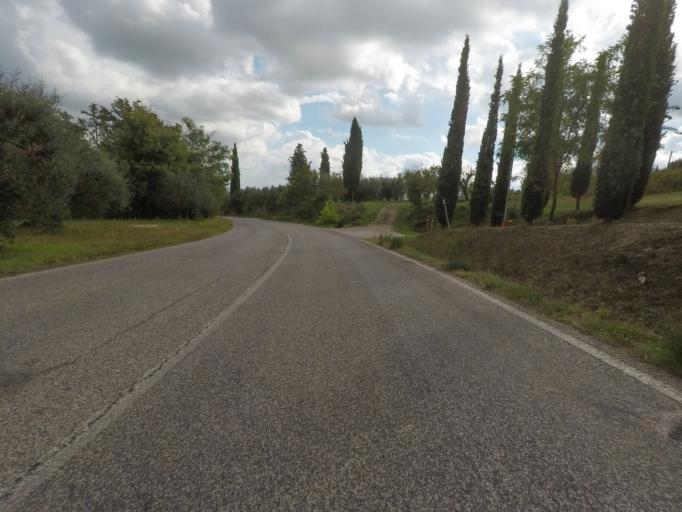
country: IT
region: Tuscany
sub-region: Provincia di Siena
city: Torrita di Siena
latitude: 43.1509
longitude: 11.7789
